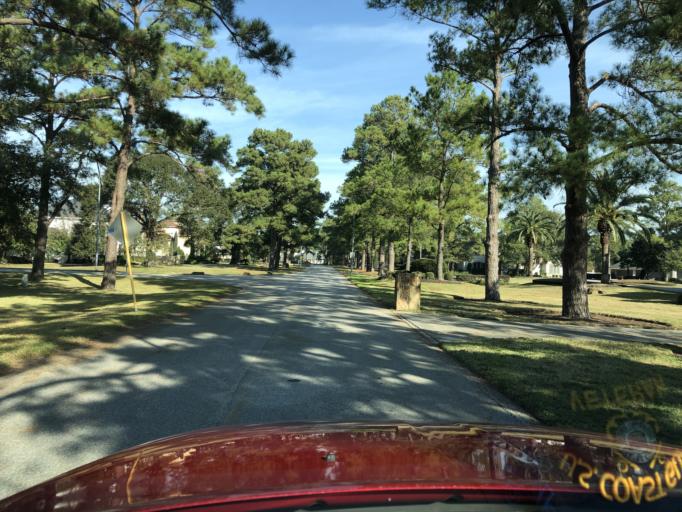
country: US
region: Texas
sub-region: Harris County
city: Tomball
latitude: 30.0392
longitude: -95.5575
